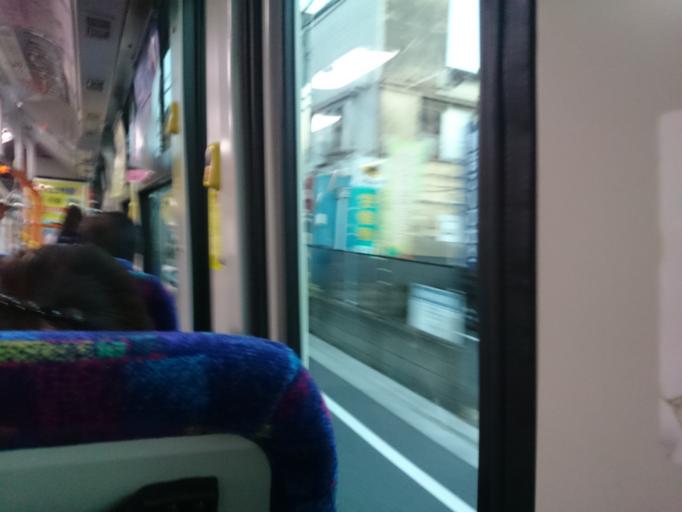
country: JP
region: Tokyo
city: Mitaka-shi
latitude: 35.6941
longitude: 139.6191
